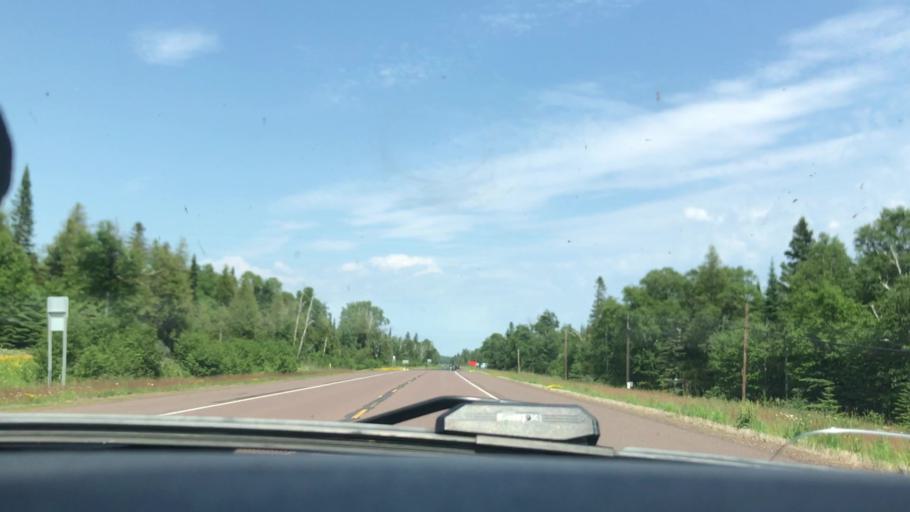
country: US
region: Minnesota
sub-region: Cook County
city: Grand Marais
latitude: 47.6285
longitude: -90.7312
